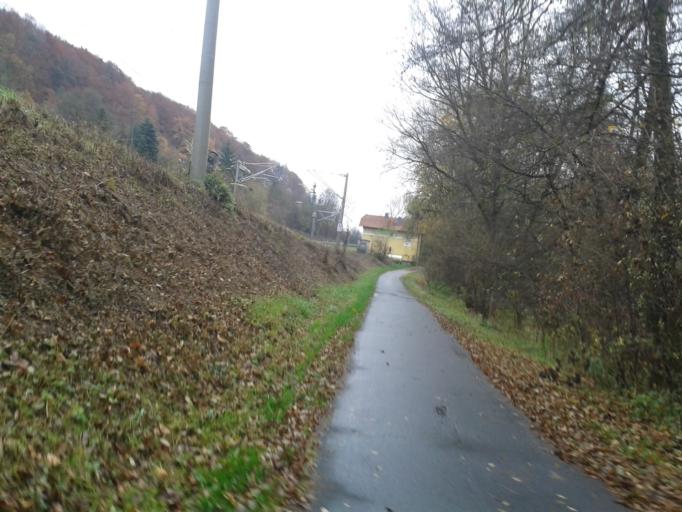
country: DE
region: Bavaria
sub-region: Regierungsbezirk Mittelfranken
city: Pommelsbrunn
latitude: 49.5011
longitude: 11.5159
